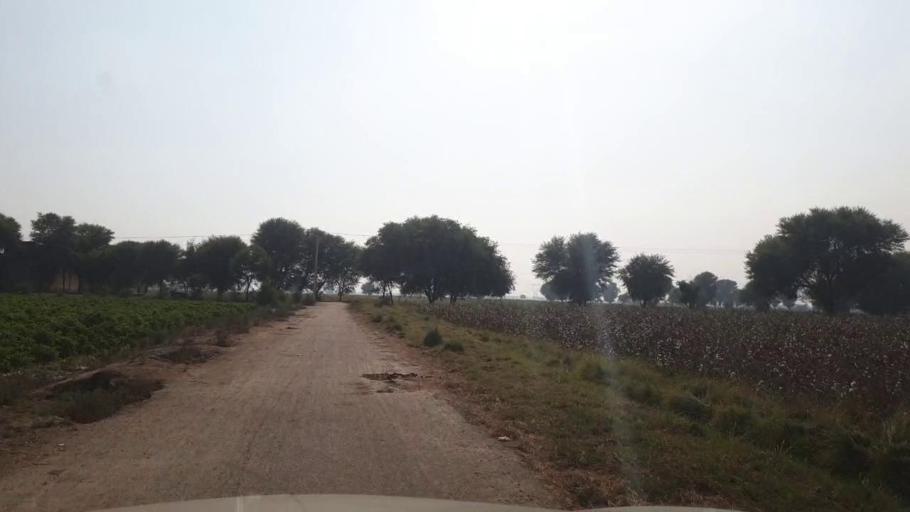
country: PK
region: Sindh
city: Bhan
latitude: 26.5419
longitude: 67.7515
